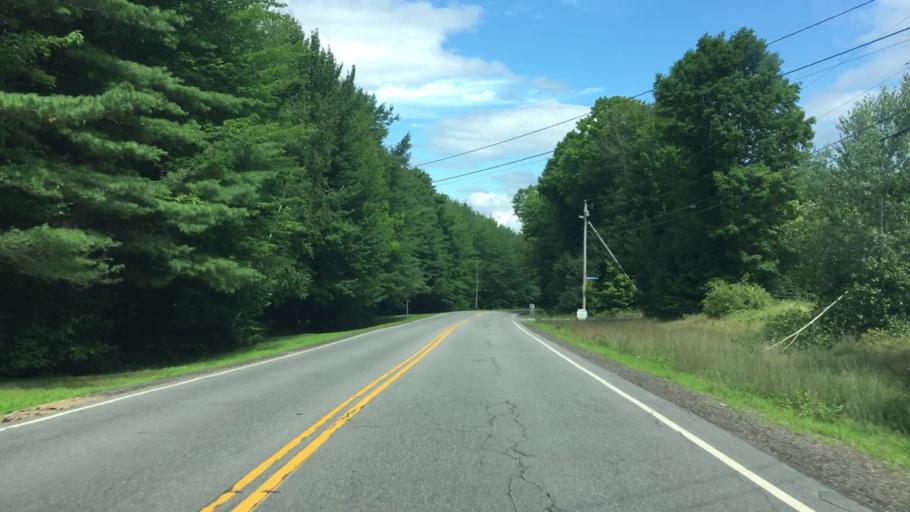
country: US
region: New Hampshire
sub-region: Belknap County
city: Meredith
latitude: 43.5869
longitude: -71.5174
